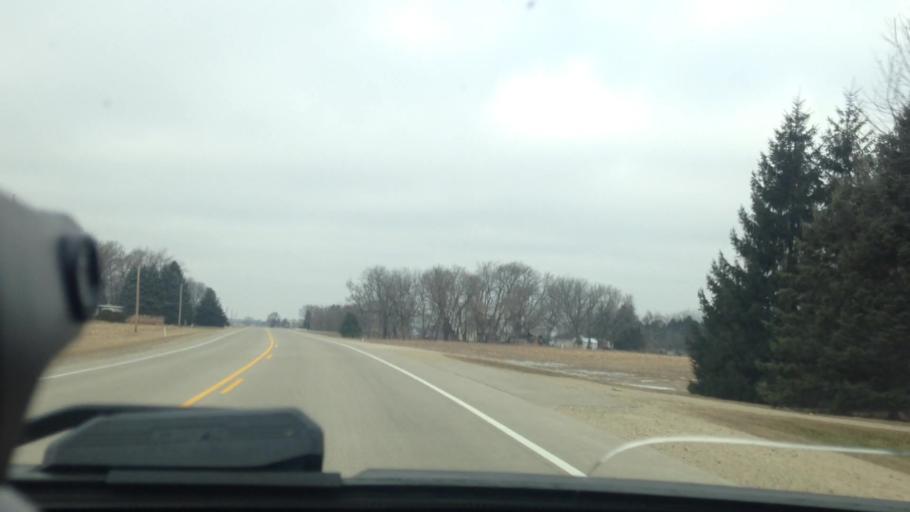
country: US
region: Wisconsin
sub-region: Dodge County
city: Horicon
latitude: 43.4648
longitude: -88.6660
